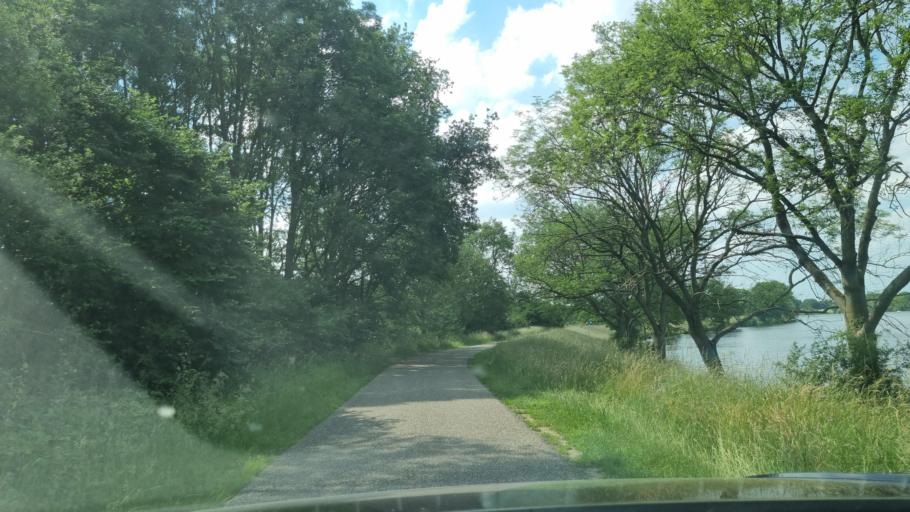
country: NL
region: North Brabant
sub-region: Gemeente Cuijk
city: Cuijk
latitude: 51.7371
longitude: 5.9040
